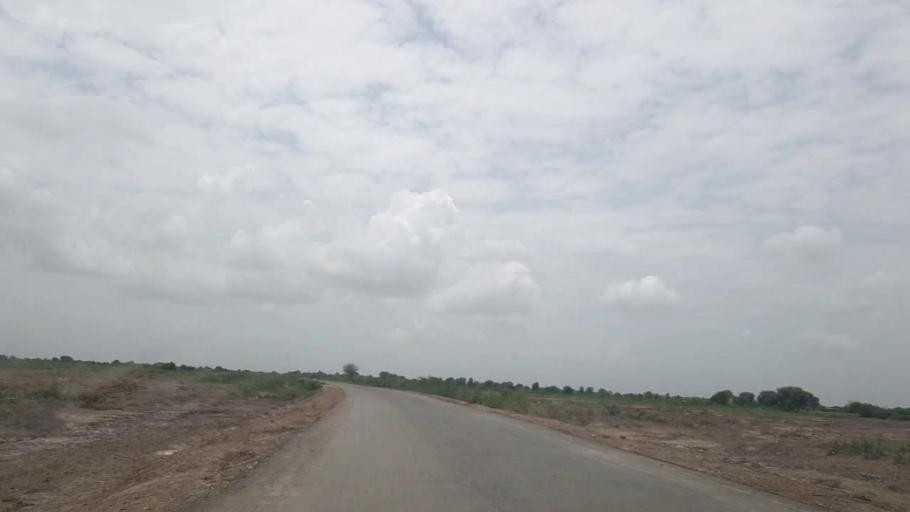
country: PK
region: Sindh
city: Naukot
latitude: 24.9459
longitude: 69.2802
